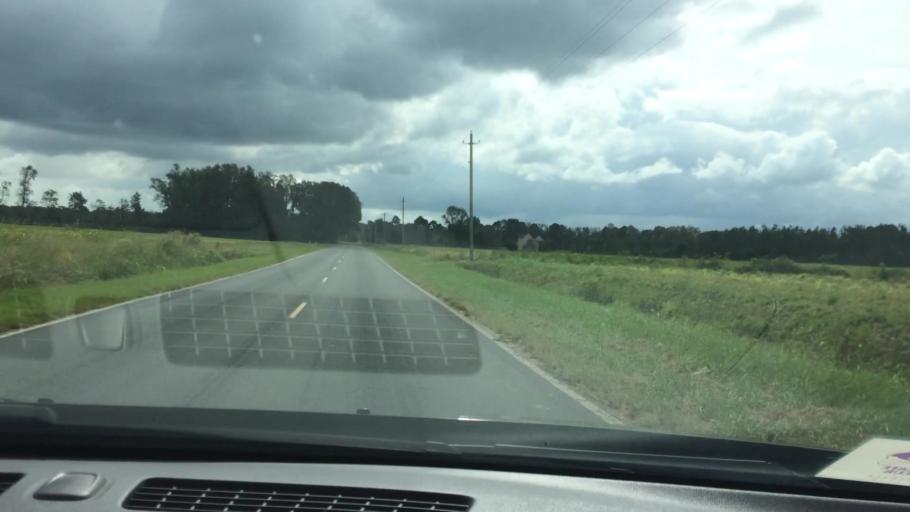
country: US
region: North Carolina
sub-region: Pitt County
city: Farmville
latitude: 35.5432
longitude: -77.5450
